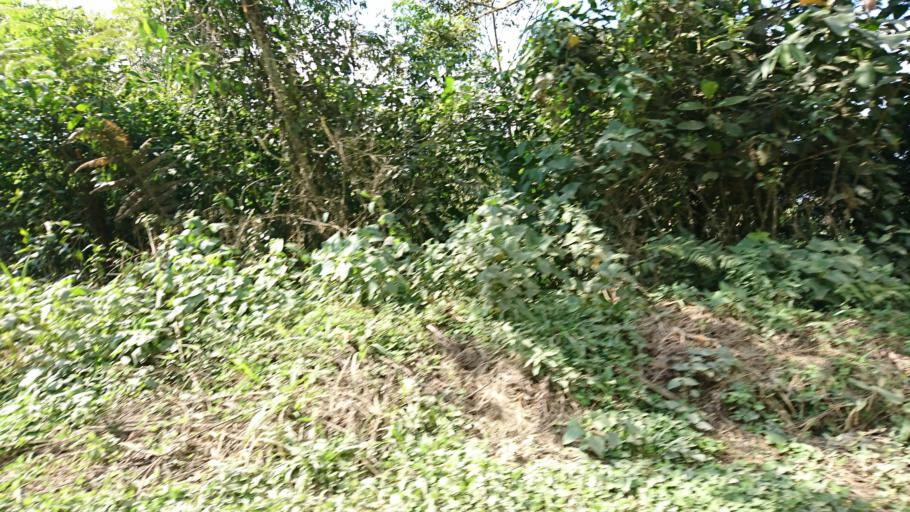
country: BO
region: La Paz
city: Coroico
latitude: -16.1322
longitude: -67.7518
